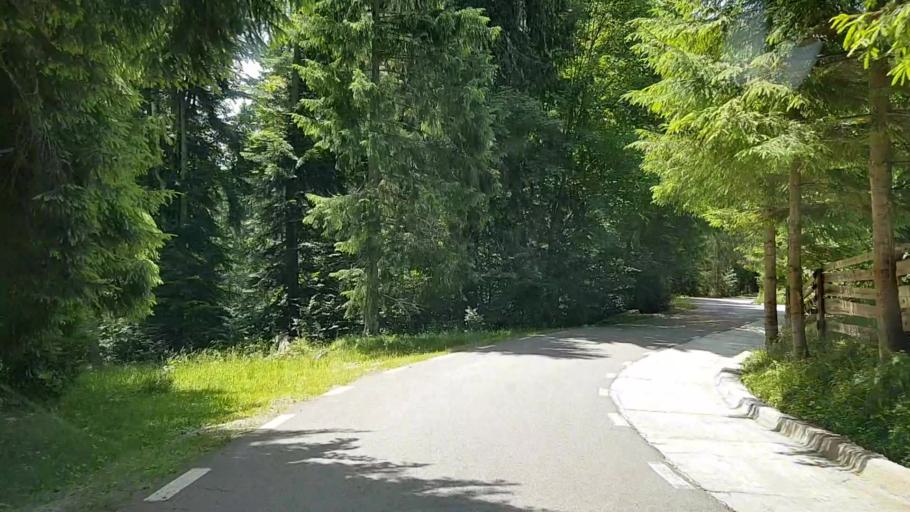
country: RO
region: Suceava
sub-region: Comuna Crucea
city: Crucea
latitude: 47.4272
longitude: 25.5807
